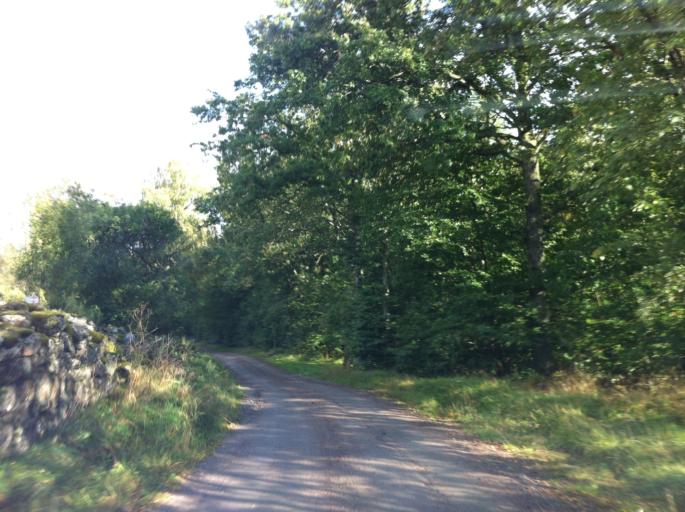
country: SE
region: Skane
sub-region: Hassleholms Kommun
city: Sosdala
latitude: 56.1280
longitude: 13.5881
